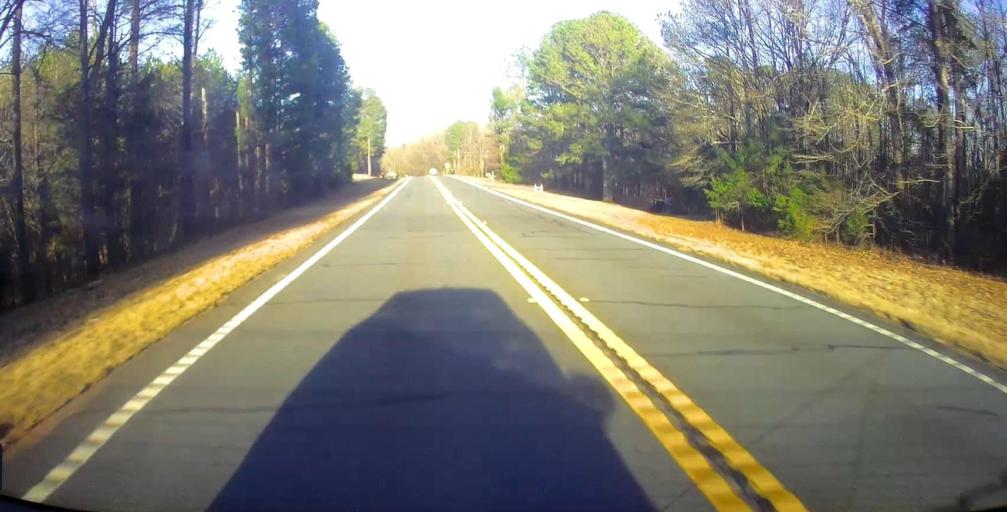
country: US
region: Georgia
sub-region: Talbot County
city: Talbotton
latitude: 32.7890
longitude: -84.5113
